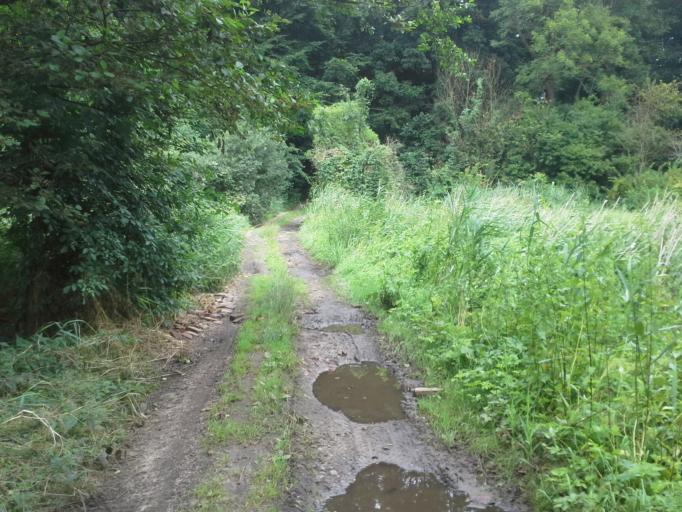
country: PL
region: Lubusz
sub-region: Powiat swiebodzinski
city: Lubrza
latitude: 52.2584
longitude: 15.3886
